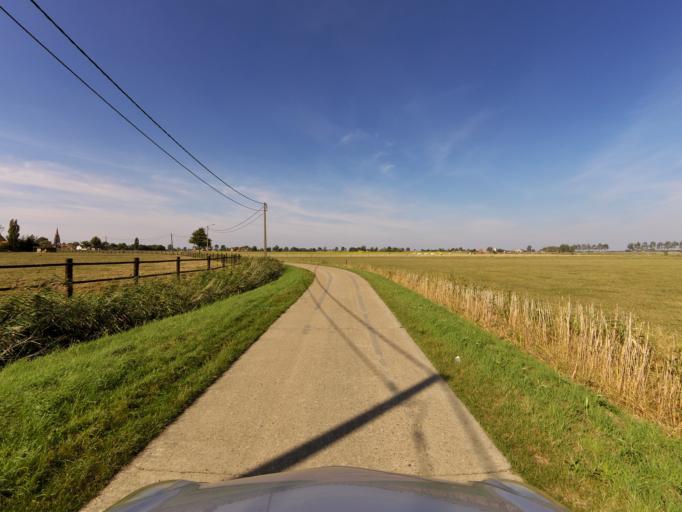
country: BE
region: Flanders
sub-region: Provincie West-Vlaanderen
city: Diksmuide
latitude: 51.1096
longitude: 2.8501
